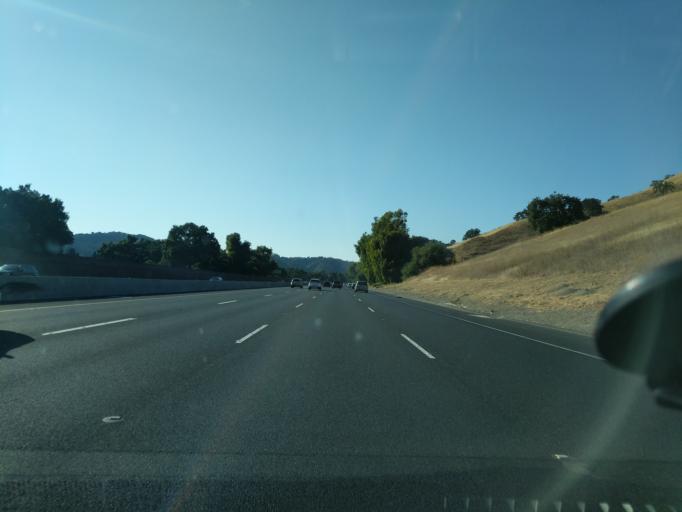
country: US
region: California
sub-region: Contra Costa County
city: Alamo
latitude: 37.8416
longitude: -122.0198
